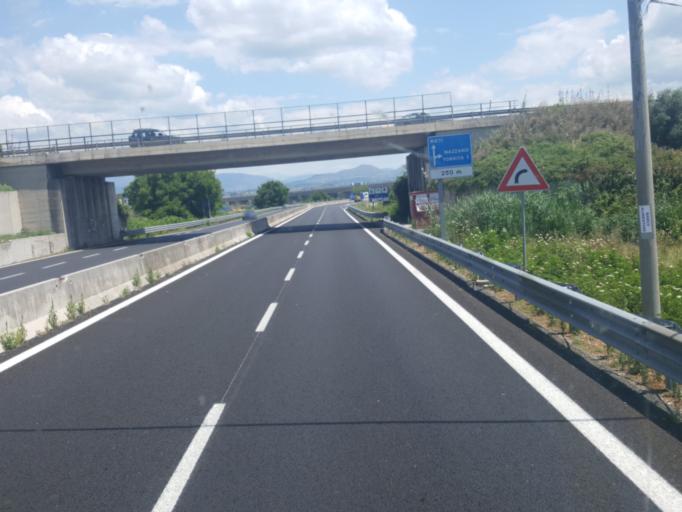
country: IT
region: Latium
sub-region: Citta metropolitana di Roma Capitale
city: Fiano Romano
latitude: 42.1465
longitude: 12.6184
